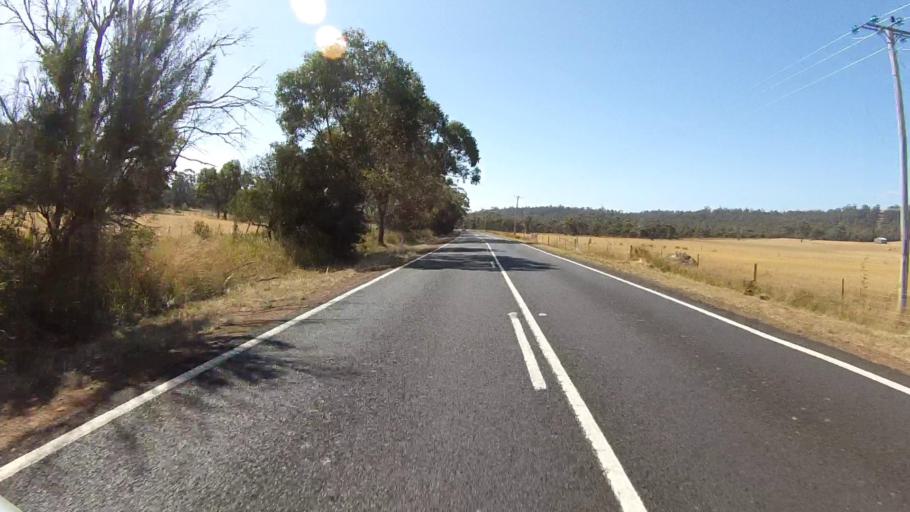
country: AU
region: Tasmania
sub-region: Sorell
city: Sorell
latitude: -42.4208
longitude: 147.9348
